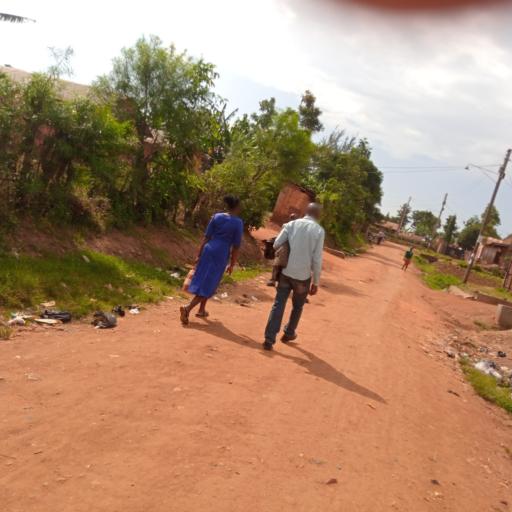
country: UG
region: Eastern Region
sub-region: Mbale District
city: Mbale
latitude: 1.0938
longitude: 34.1780
